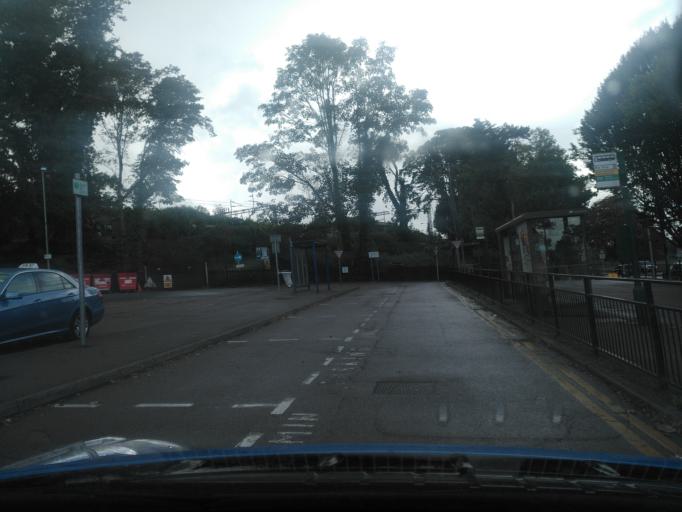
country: GB
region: England
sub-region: Hertfordshire
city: Hemel Hempstead
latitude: 51.7428
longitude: -0.4906
